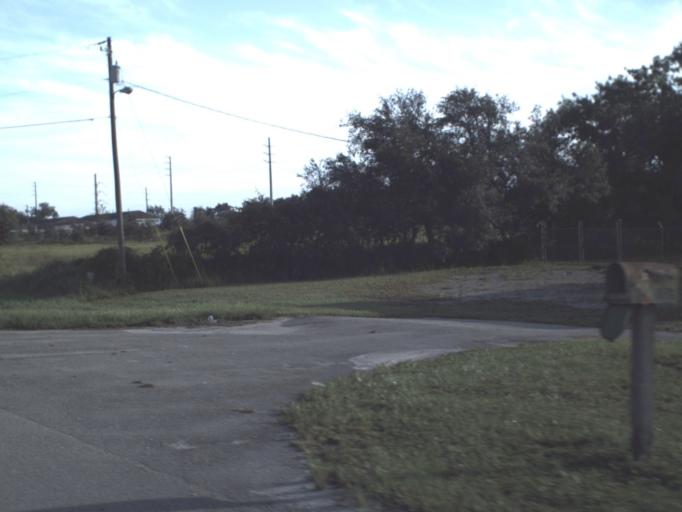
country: US
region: Florida
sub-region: Highlands County
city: Sebring
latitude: 27.4382
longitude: -81.4188
